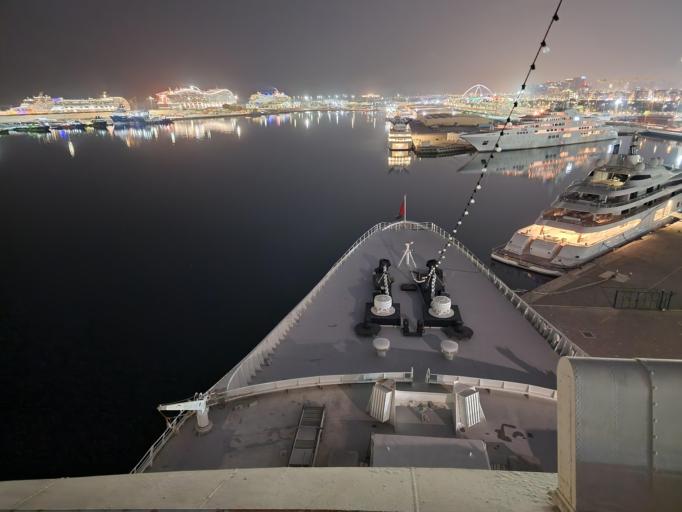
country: AE
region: Ash Shariqah
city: Sharjah
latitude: 25.2628
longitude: 55.2814
